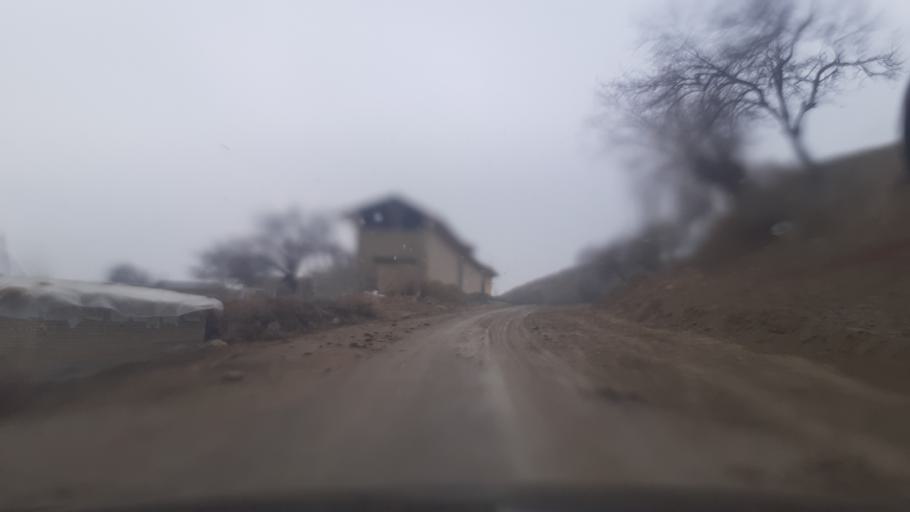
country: UZ
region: Namangan
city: Yangiqo`rg`on
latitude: 41.1110
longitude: 71.6720
